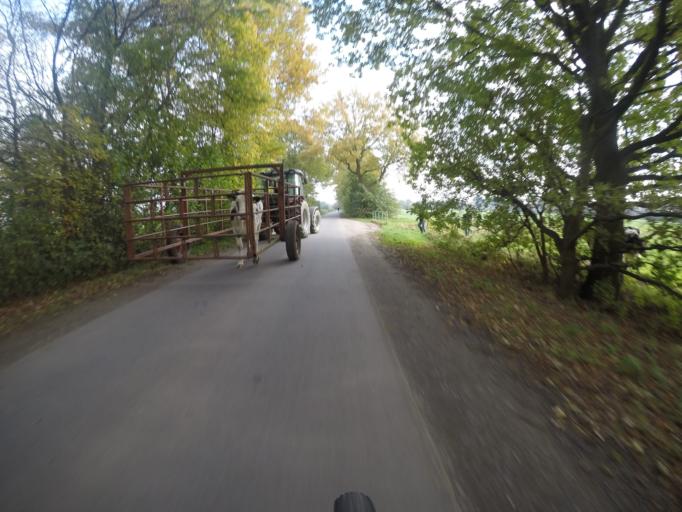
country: DE
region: North Rhine-Westphalia
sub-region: Regierungsbezirk Dusseldorf
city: Bocholt
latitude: 51.8354
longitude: 6.5469
